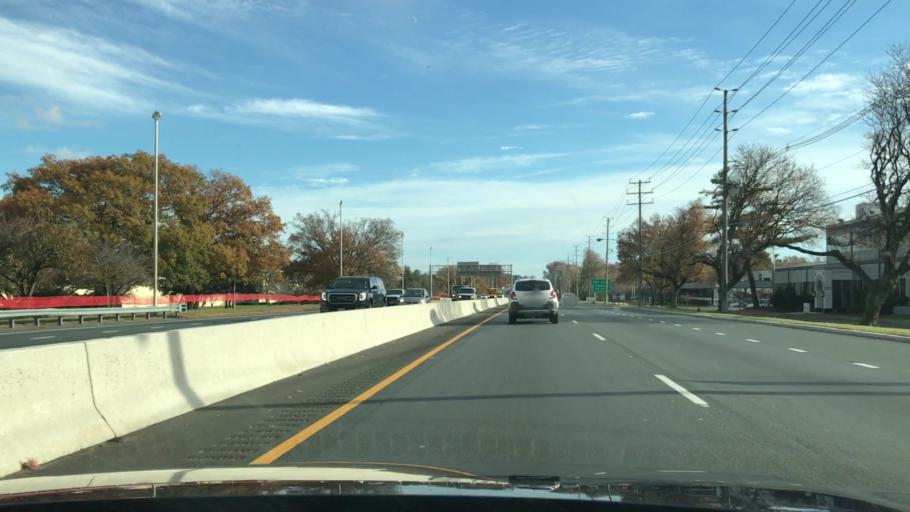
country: US
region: New Jersey
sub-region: Bergen County
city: Fair Lawn
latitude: 40.9482
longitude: -74.1352
